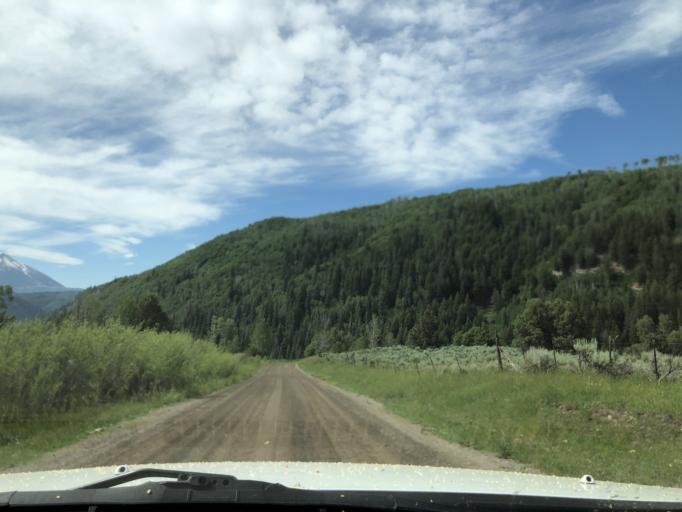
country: US
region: Colorado
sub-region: Delta County
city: Paonia
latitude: 38.9959
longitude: -107.3533
